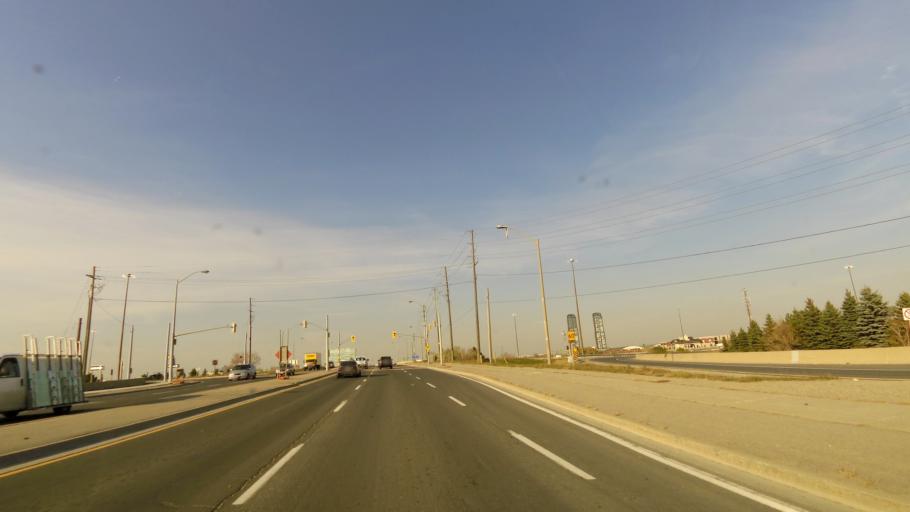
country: CA
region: Ontario
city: Concord
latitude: 43.7839
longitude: -79.5221
